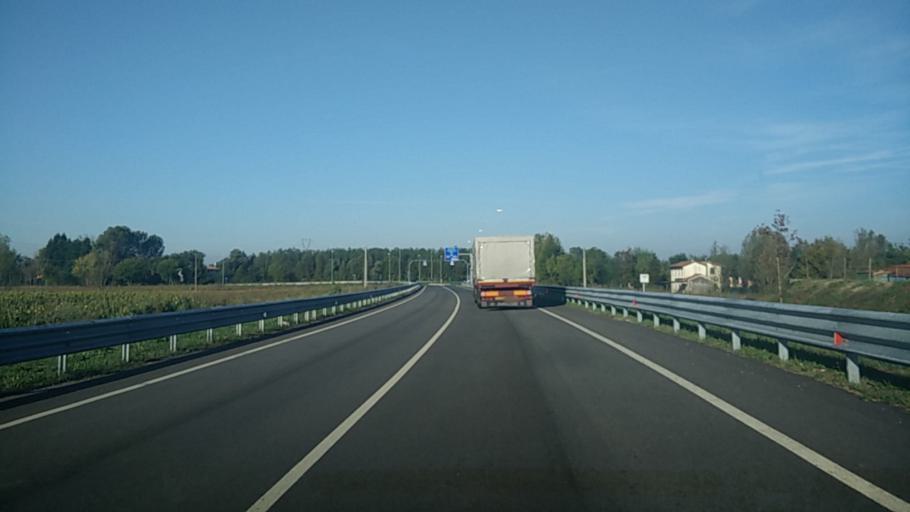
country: IT
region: Veneto
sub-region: Provincia di Venezia
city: Peseggia-Gardigiano
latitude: 45.5510
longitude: 12.1748
